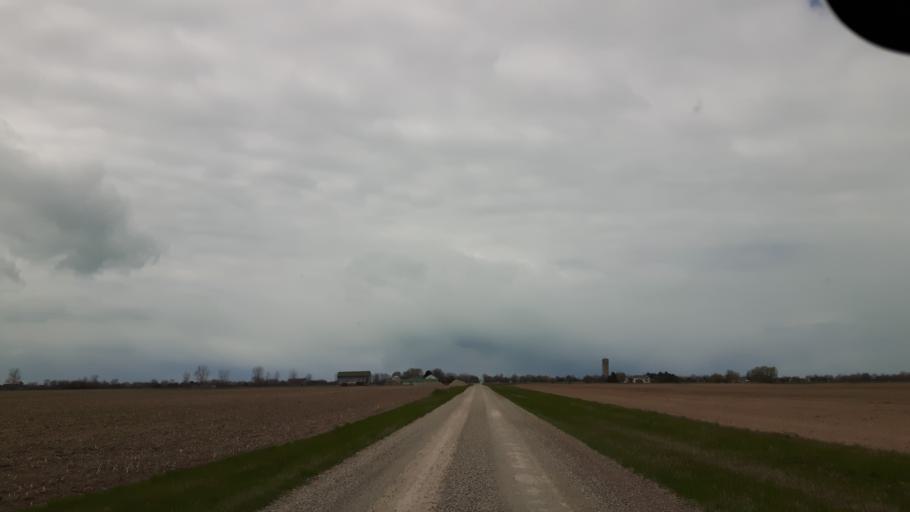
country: CA
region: Ontario
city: Bluewater
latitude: 43.4726
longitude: -81.6899
